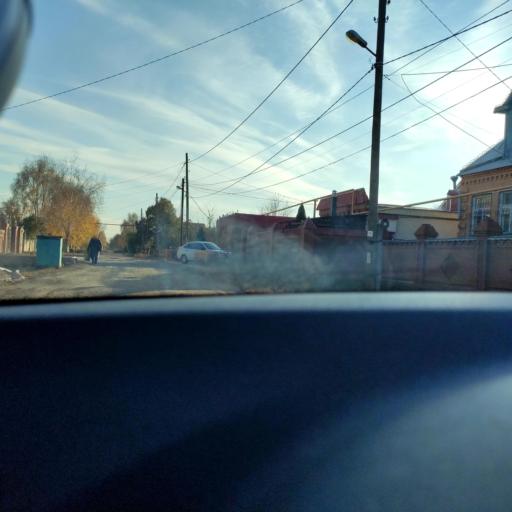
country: RU
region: Samara
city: Petra-Dubrava
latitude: 53.2558
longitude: 50.3243
